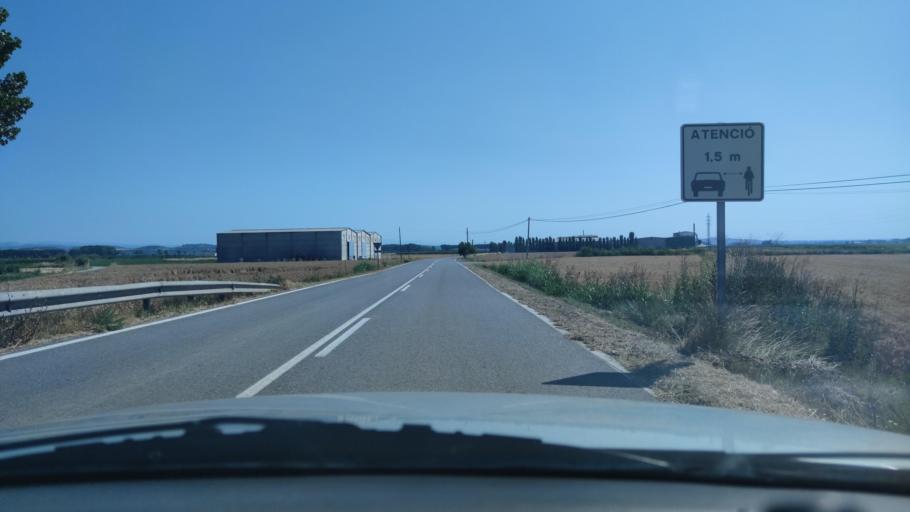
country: ES
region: Catalonia
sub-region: Provincia de Lleida
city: Linyola
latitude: 41.7153
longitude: 0.9090
